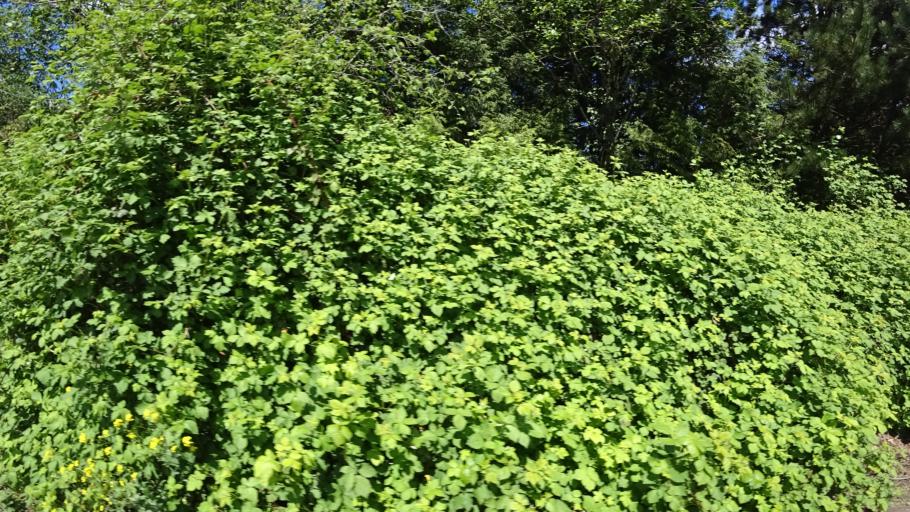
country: US
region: Oregon
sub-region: Washington County
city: West Haven
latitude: 45.5517
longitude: -122.7723
